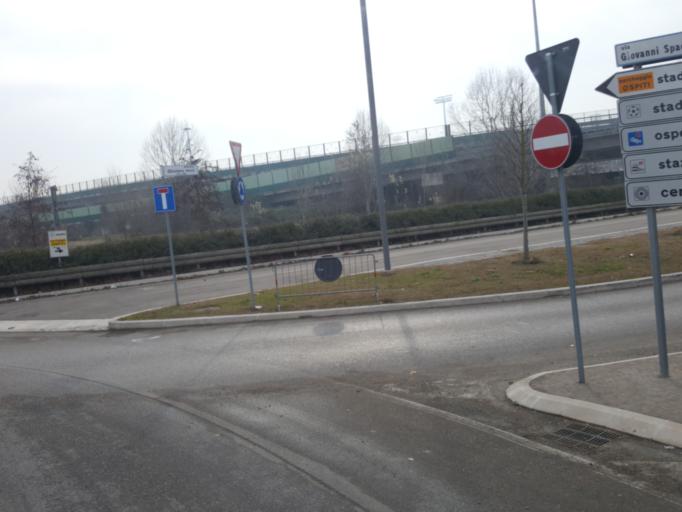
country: IT
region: Emilia-Romagna
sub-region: Forli-Cesena
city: Cesena
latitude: 44.1437
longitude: 12.2632
